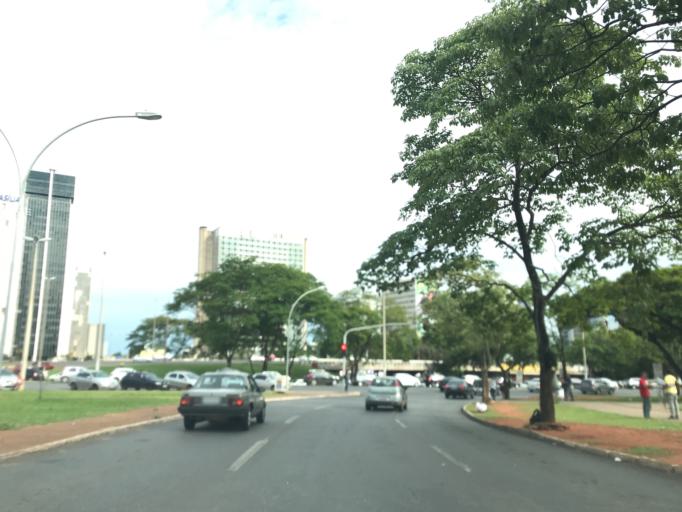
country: BR
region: Federal District
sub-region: Brasilia
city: Brasilia
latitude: -15.7974
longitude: -47.8853
